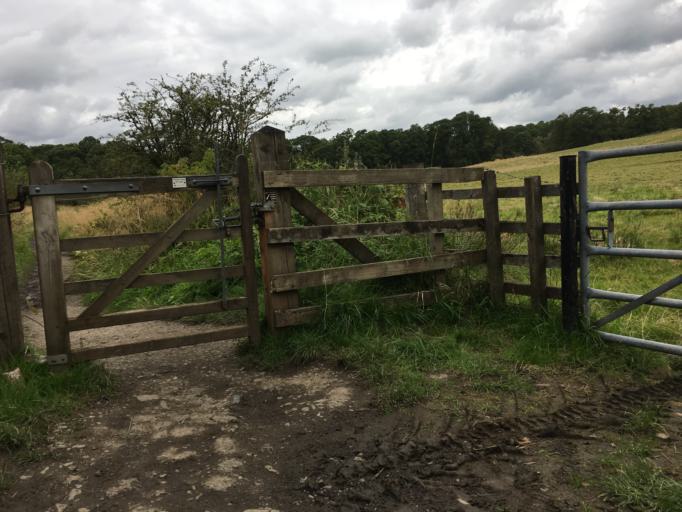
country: GB
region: Scotland
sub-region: Stirling
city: Killearn
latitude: 56.0354
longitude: -4.3920
